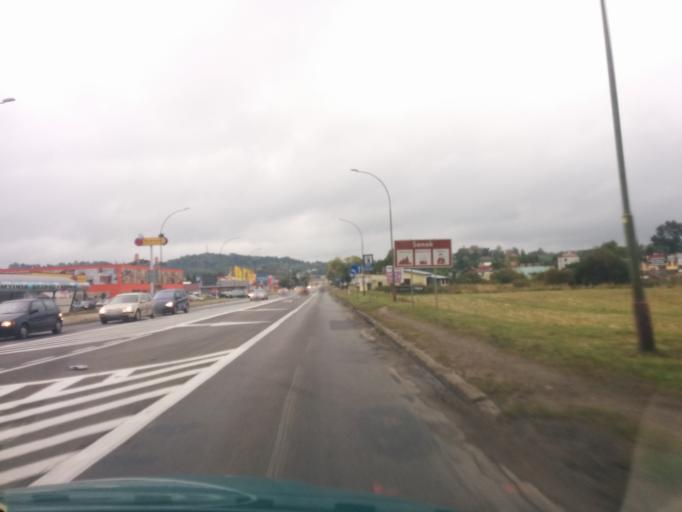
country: PL
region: Subcarpathian Voivodeship
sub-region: Powiat sanocki
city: Sanok
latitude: 49.5694
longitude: 22.1533
